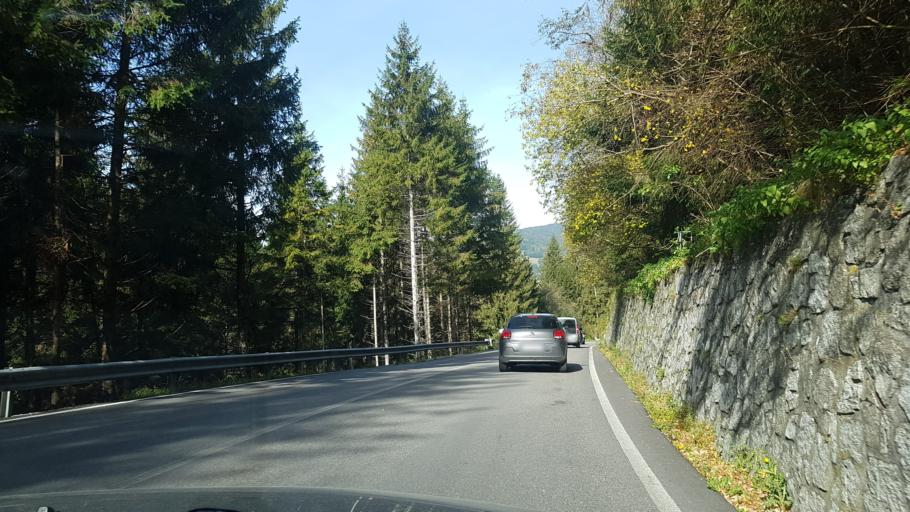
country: IT
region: Veneto
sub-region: Provincia di Belluno
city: San Nicolo Comelico
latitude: 46.5711
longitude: 12.5357
